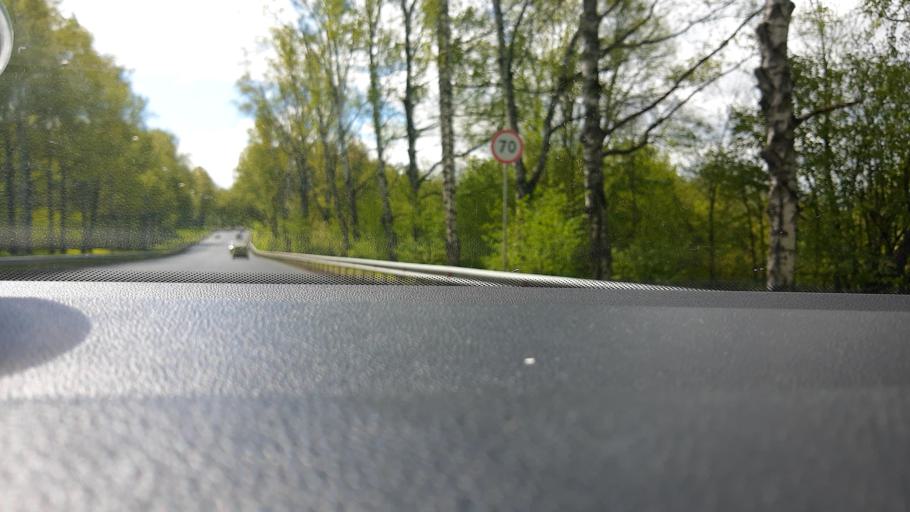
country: RU
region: Moskovskaya
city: Yakhroma
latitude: 56.3062
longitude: 37.4920
